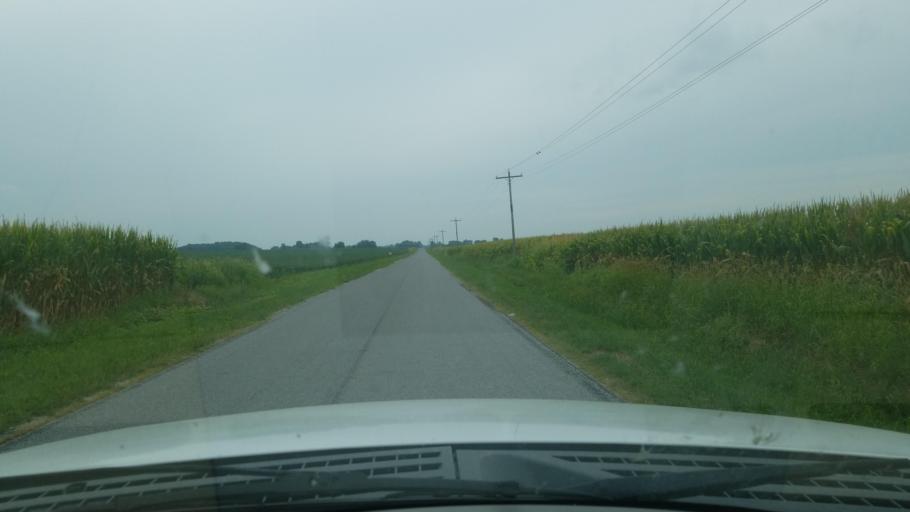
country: US
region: Illinois
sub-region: Saline County
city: Eldorado
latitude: 37.8671
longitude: -88.4709
